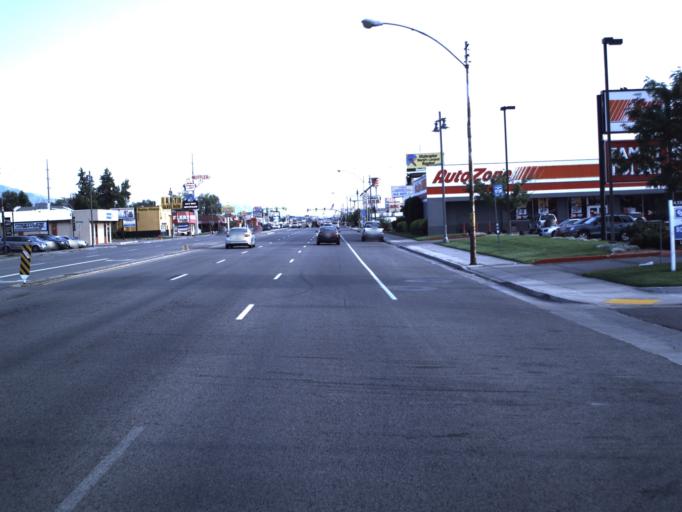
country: US
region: Utah
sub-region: Salt Lake County
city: Centerfield
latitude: 40.6899
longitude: -111.8884
